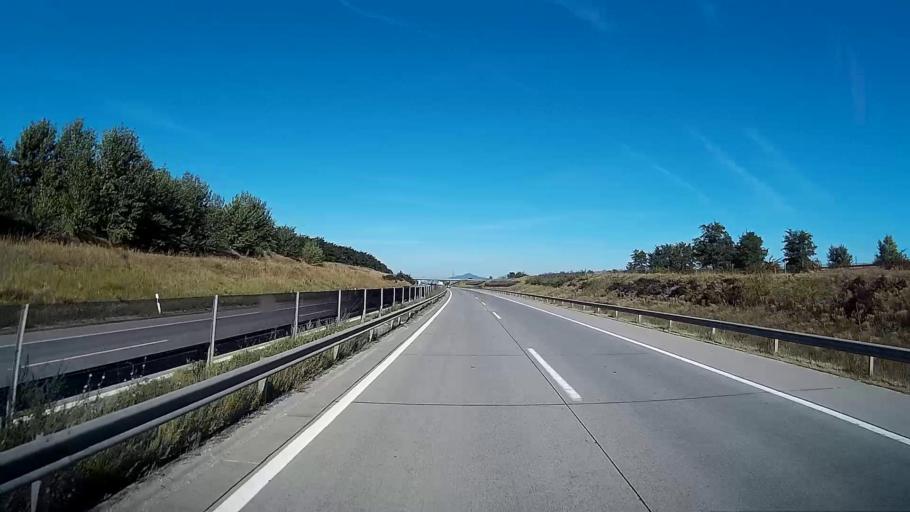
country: HU
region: Pest
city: Csomor
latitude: 47.5443
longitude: 19.2048
